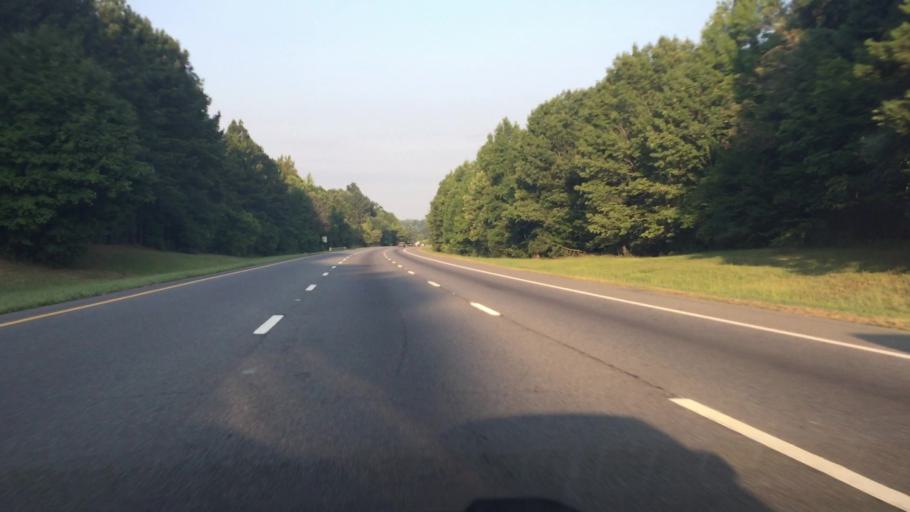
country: US
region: North Carolina
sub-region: Davidson County
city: Lexington
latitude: 35.7904
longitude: -80.2266
